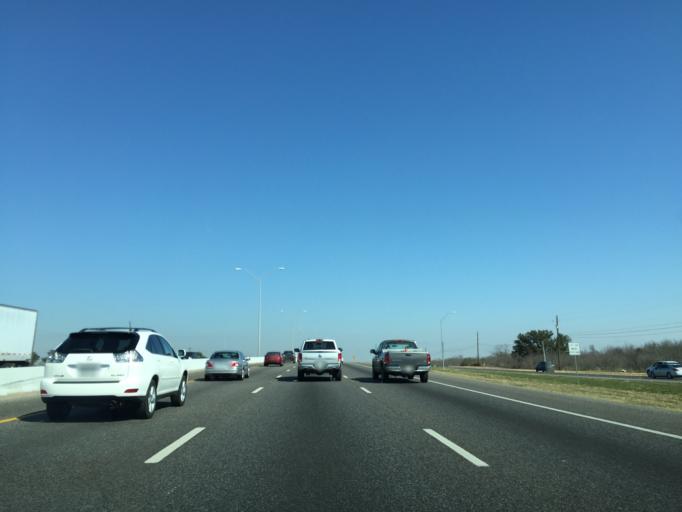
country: US
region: Texas
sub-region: Williamson County
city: Georgetown
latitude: 30.5856
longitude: -97.6927
